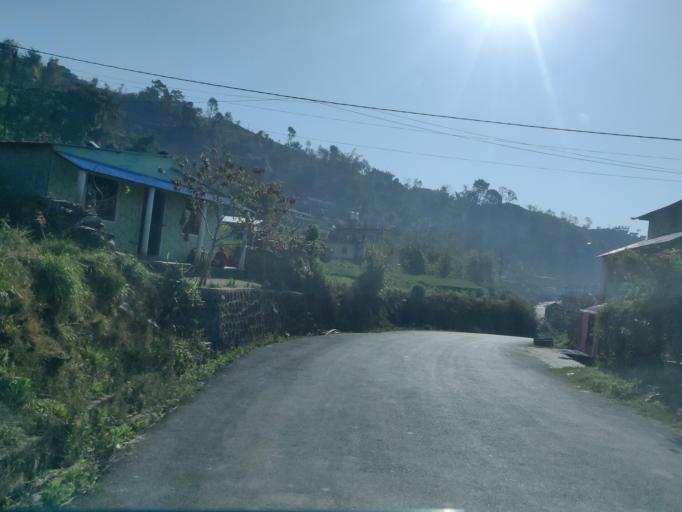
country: NP
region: Western Region
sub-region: Gandaki Zone
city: Pokhara
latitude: 28.2373
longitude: 83.9639
